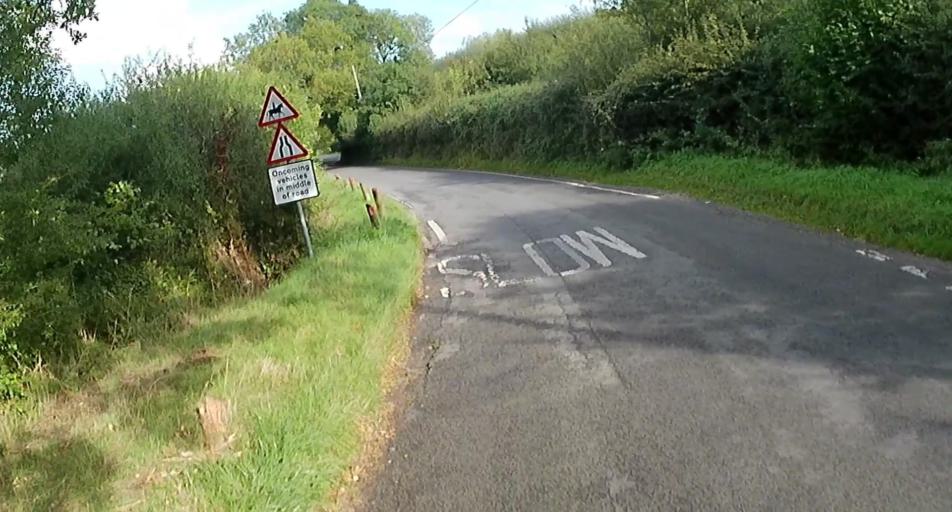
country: GB
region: England
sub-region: Hampshire
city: Tadley
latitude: 51.3315
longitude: -1.1738
